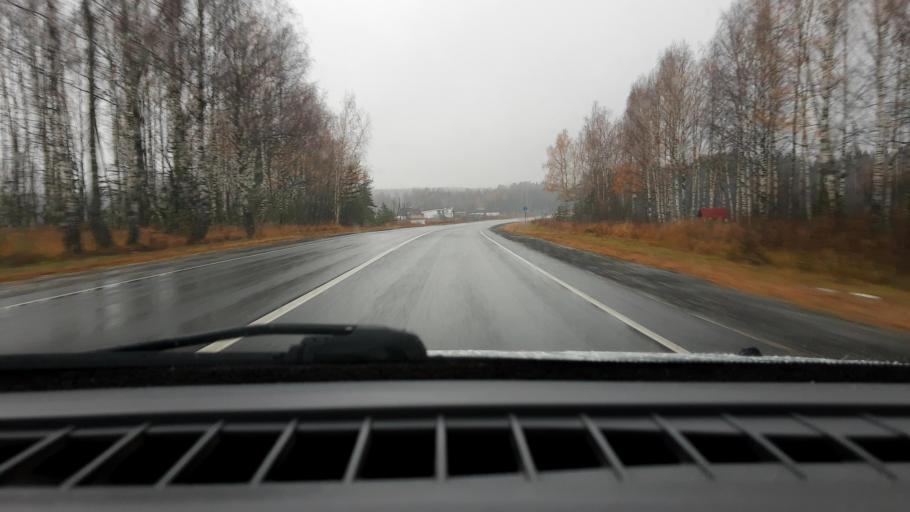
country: RU
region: Nizjnij Novgorod
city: Linda
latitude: 56.6698
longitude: 44.1402
